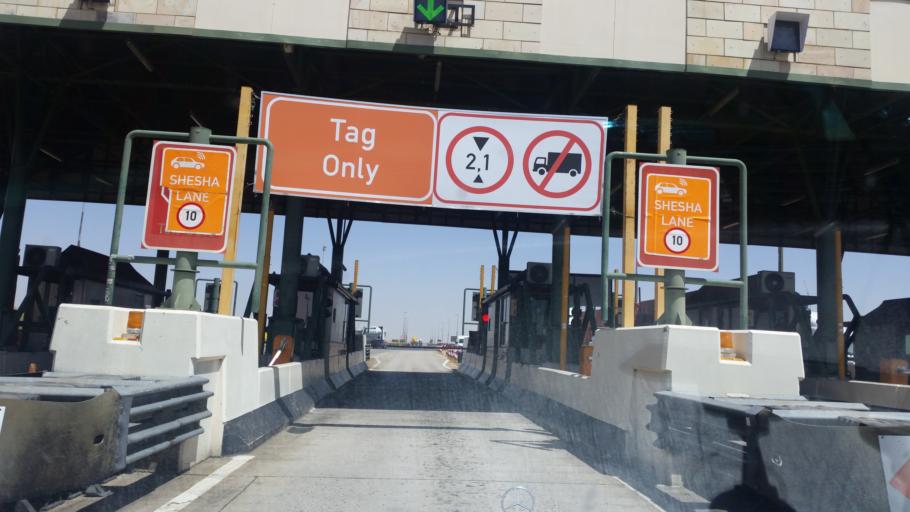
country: ZA
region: Orange Free State
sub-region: Lejweleputswa District Municipality
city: Brandfort
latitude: -28.7987
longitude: 26.6907
